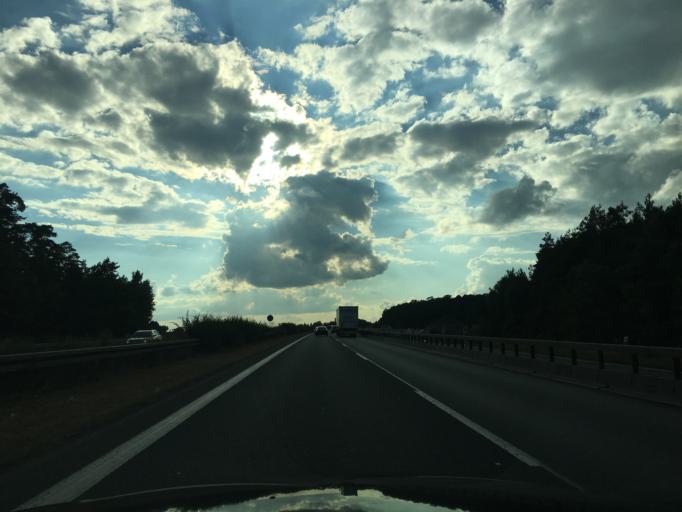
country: DE
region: Bavaria
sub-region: Regierungsbezirk Mittelfranken
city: Burgoberbach
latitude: 49.2589
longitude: 10.5519
